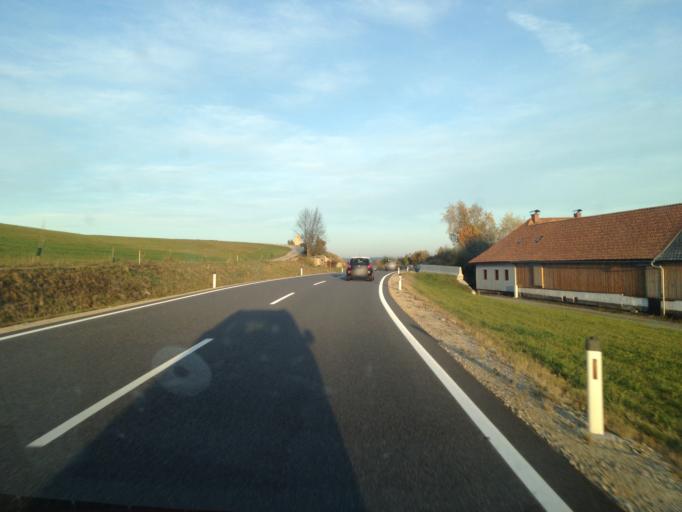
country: AT
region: Upper Austria
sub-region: Politischer Bezirk Freistadt
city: Freistadt
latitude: 48.5506
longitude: 14.6368
